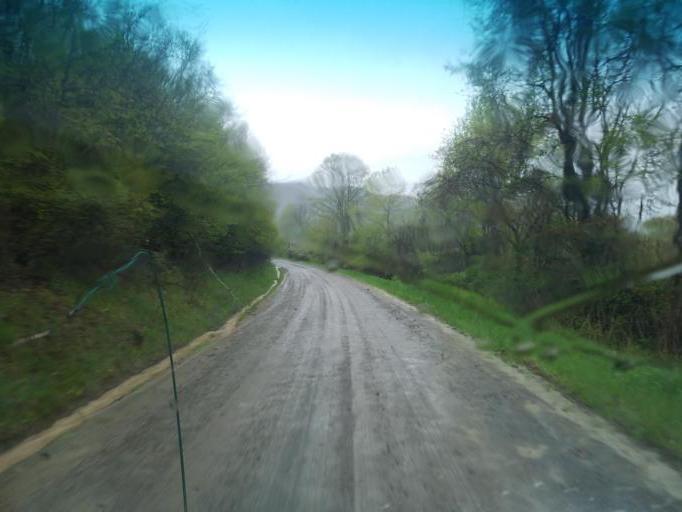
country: US
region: Pennsylvania
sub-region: Tioga County
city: Westfield
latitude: 41.9146
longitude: -77.6287
